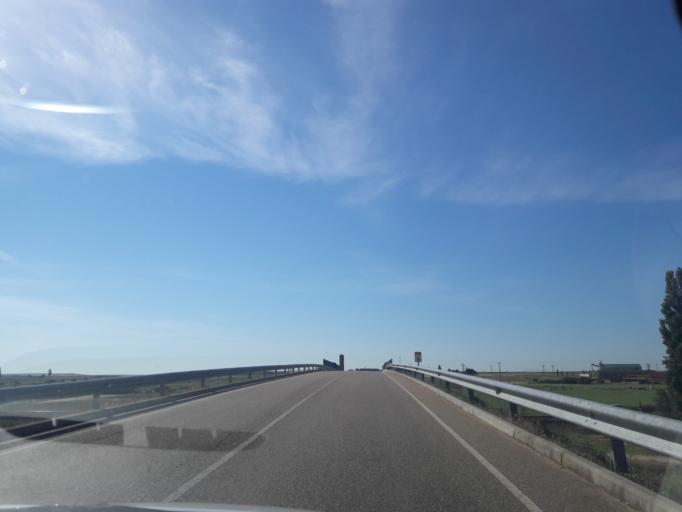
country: ES
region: Castille and Leon
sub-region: Provincia de Salamanca
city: Espino de la Orbada
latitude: 41.0845
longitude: -5.3973
